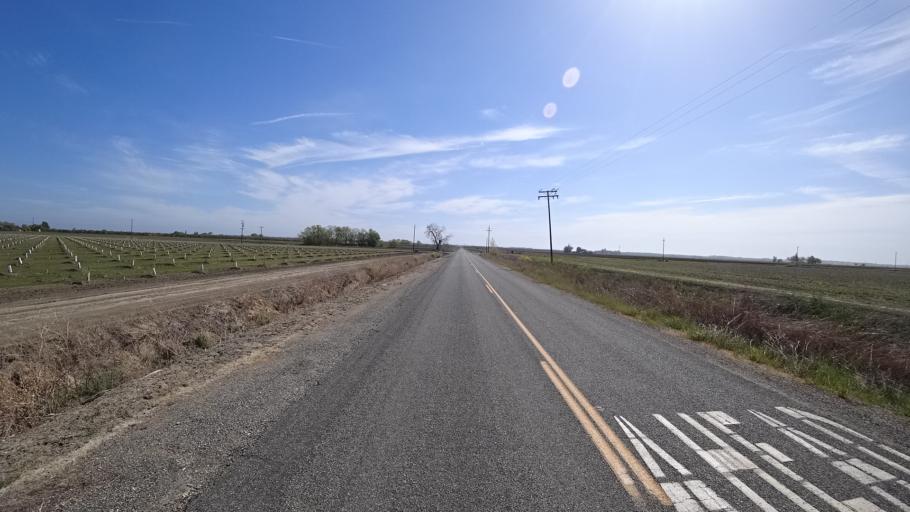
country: US
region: California
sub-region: Glenn County
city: Hamilton City
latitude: 39.6162
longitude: -122.0387
